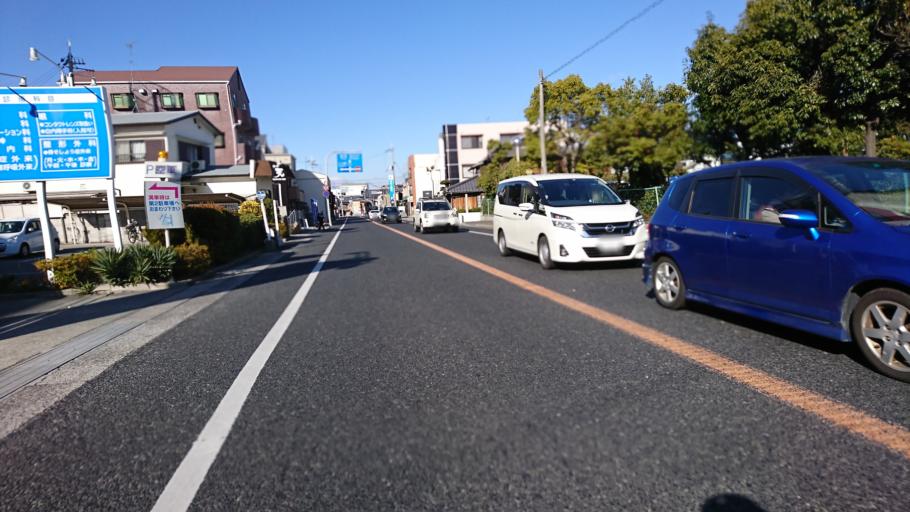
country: JP
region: Hyogo
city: Kakogawacho-honmachi
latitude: 34.7207
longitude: 134.8920
